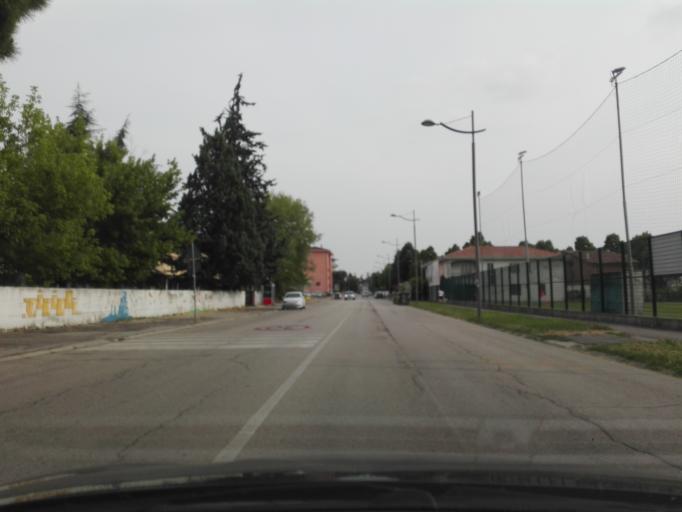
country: IT
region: Veneto
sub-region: Provincia di Rovigo
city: Rovigo
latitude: 45.0782
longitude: 11.7979
